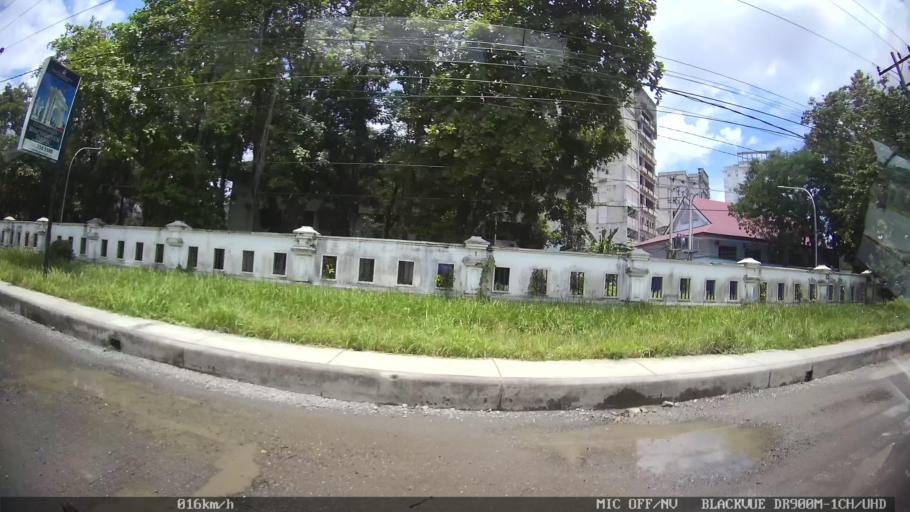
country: ID
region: North Sumatra
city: Medan
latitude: 3.6063
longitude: 98.7146
